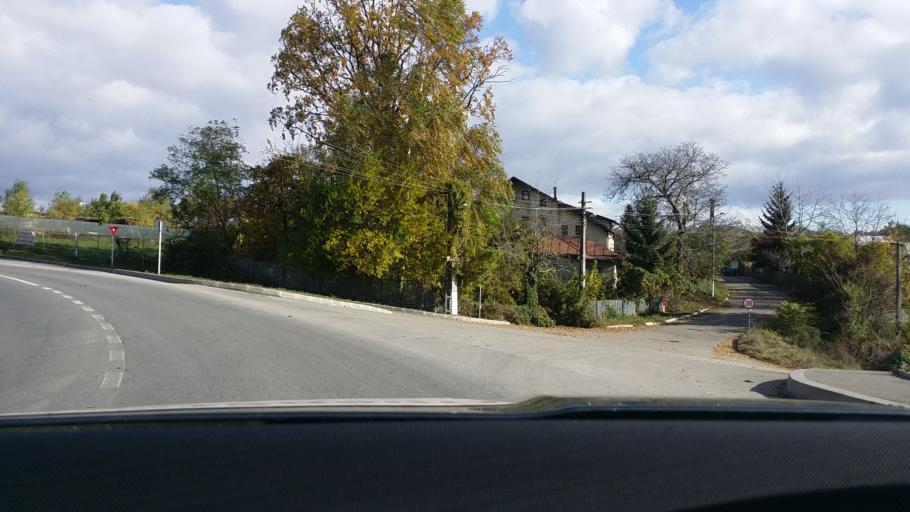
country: RO
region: Prahova
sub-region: Municipiul Campina
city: Campina
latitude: 45.1250
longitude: 25.7532
